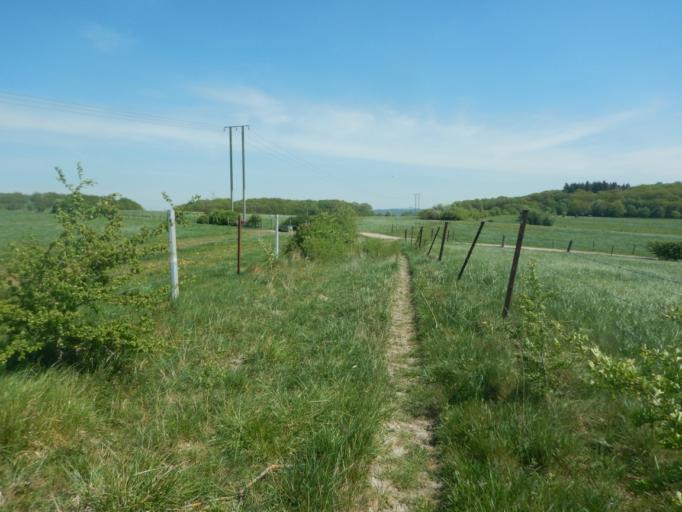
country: LU
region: Diekirch
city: Bettborn
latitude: 49.7550
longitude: 5.9311
